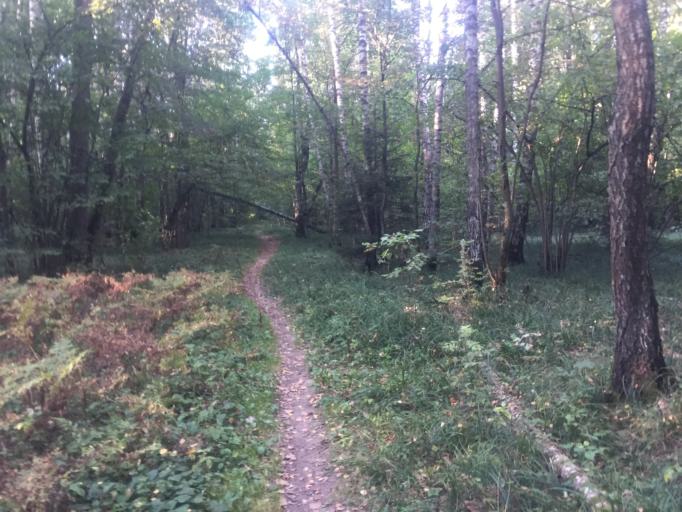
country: RU
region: Moscow
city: Gol'yanovo
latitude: 55.8427
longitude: 37.7967
